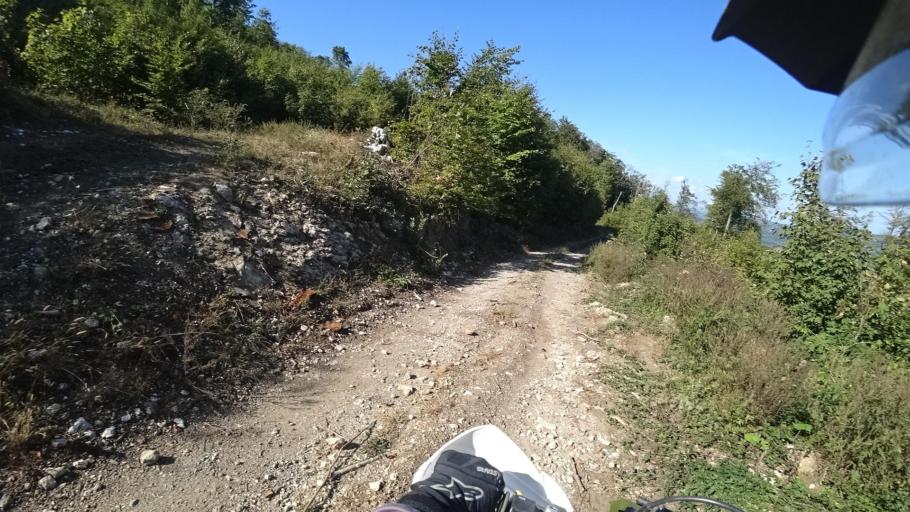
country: HR
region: Primorsko-Goranska
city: Vrbovsko
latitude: 45.2969
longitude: 15.1321
